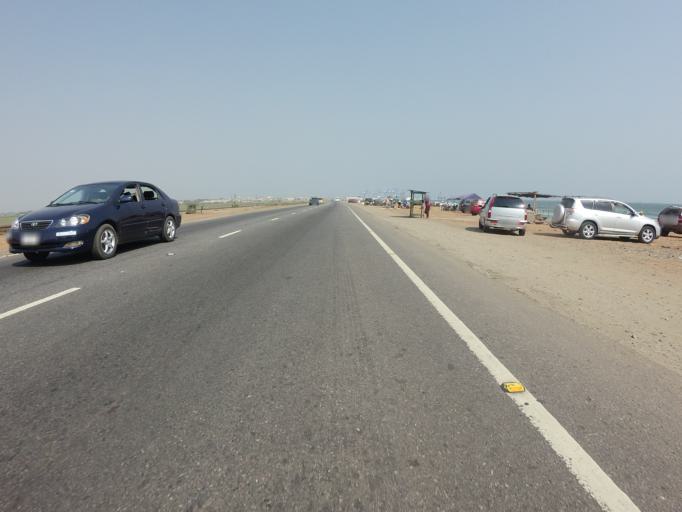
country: GH
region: Greater Accra
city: Nungua
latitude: 5.6124
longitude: -0.0414
